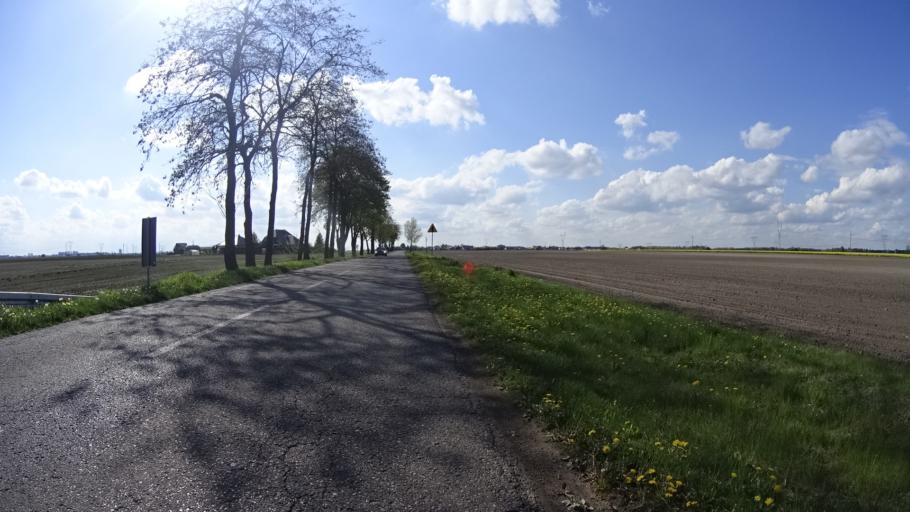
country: PL
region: Masovian Voivodeship
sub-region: Powiat warszawski zachodni
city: Jozefow
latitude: 52.2325
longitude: 20.6883
